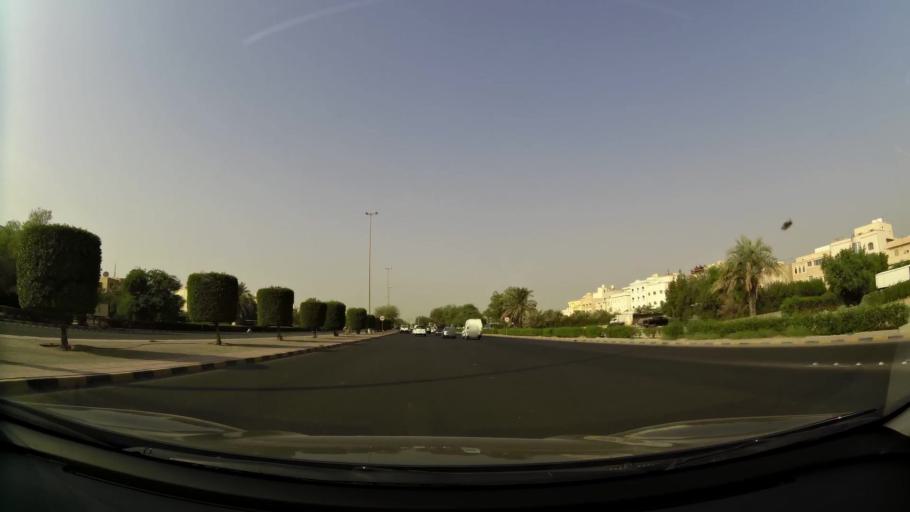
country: KW
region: Mubarak al Kabir
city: Mubarak al Kabir
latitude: 29.1803
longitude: 48.0815
